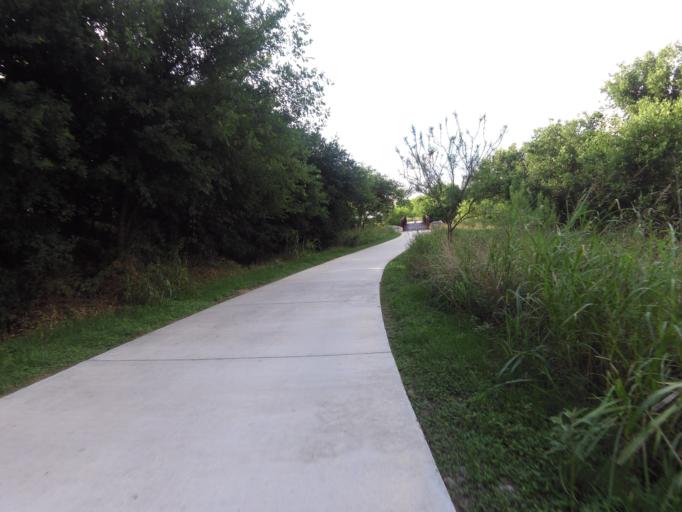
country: US
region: Texas
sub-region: Bexar County
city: Leon Valley
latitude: 29.4847
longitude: -98.6331
